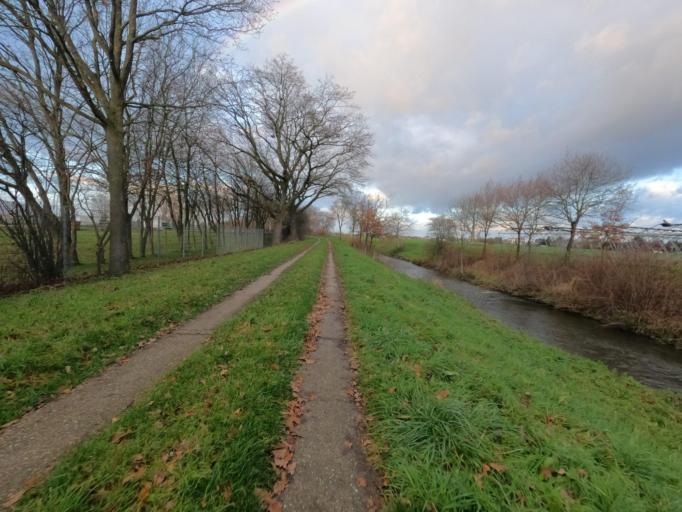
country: DE
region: North Rhine-Westphalia
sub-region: Regierungsbezirk Koln
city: Heinsberg
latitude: 51.0648
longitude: 6.1299
